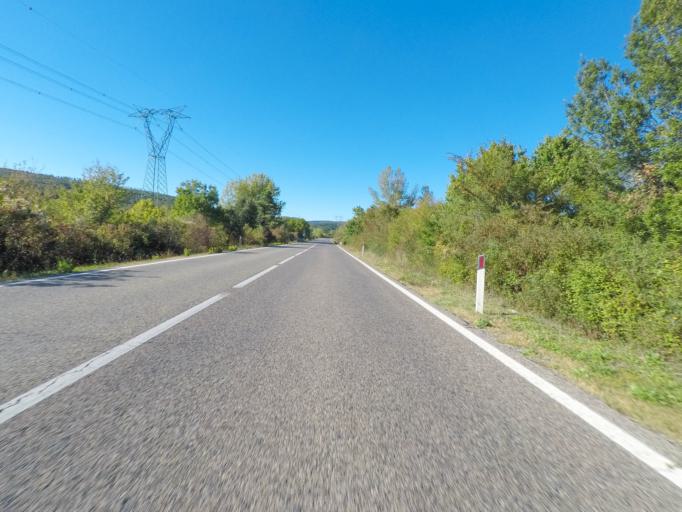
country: IT
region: Tuscany
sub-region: Provincia di Grosseto
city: Civitella Marittima
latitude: 43.0199
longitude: 11.2834
